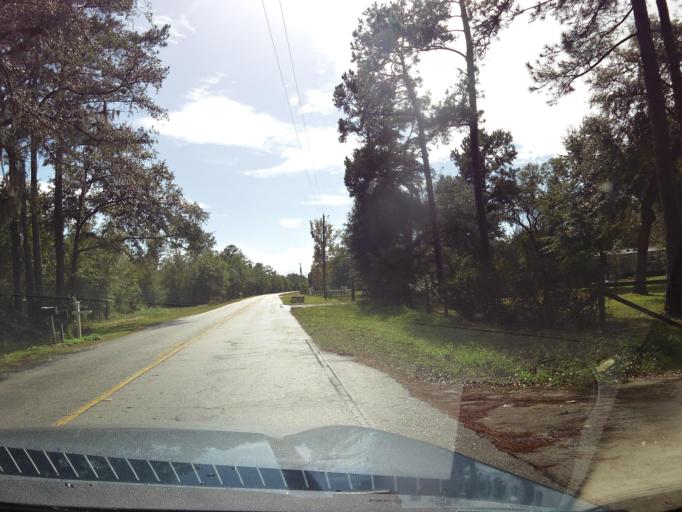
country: US
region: Florida
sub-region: Clay County
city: Asbury Lake
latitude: 29.9900
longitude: -81.8398
